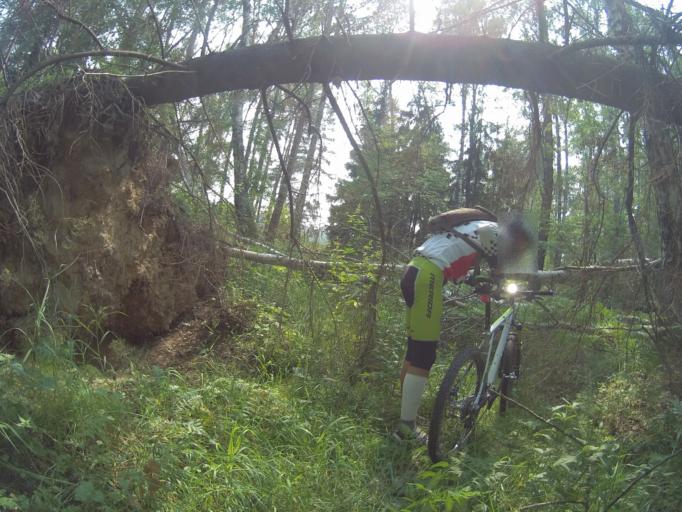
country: RU
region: Vladimir
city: Raduzhnyy
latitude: 55.9909
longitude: 40.2120
